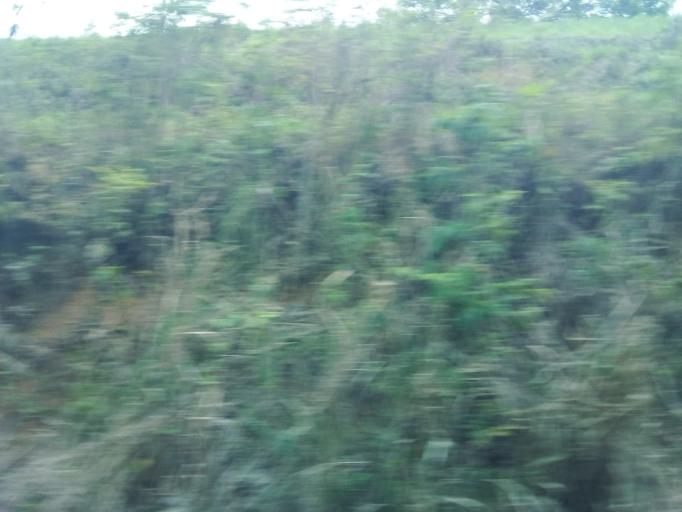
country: BR
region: Minas Gerais
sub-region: Ipatinga
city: Ipatinga
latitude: -19.4626
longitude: -42.4680
